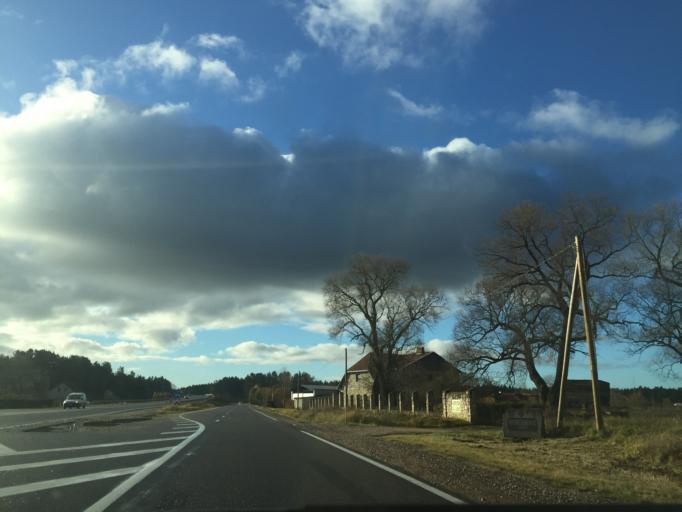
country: LV
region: Babite
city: Pinki
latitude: 56.9283
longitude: 23.9157
